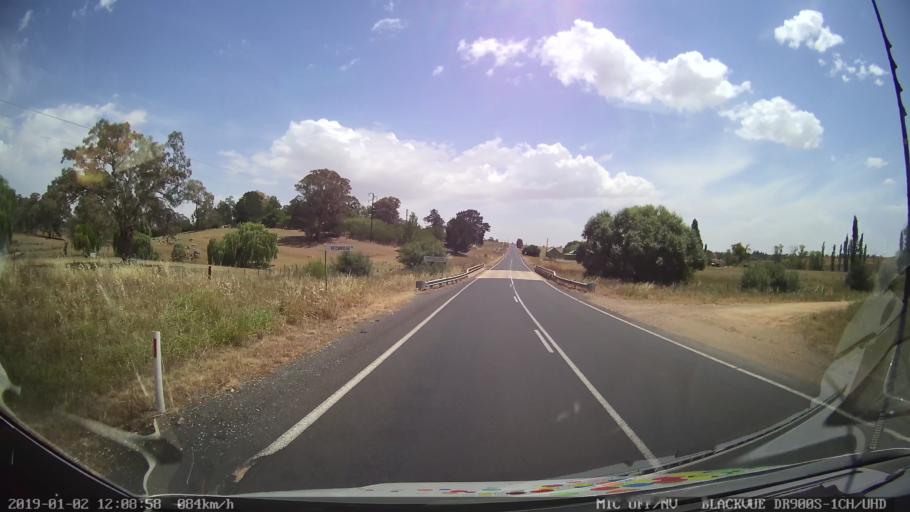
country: AU
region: New South Wales
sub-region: Young
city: Young
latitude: -34.4779
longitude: 148.2724
